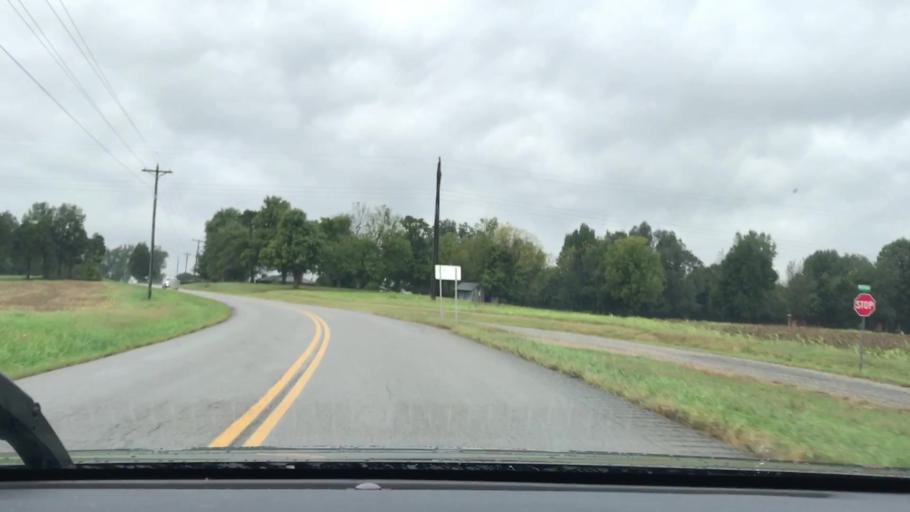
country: US
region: Kentucky
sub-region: McLean County
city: Calhoun
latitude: 37.4480
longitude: -87.2435
